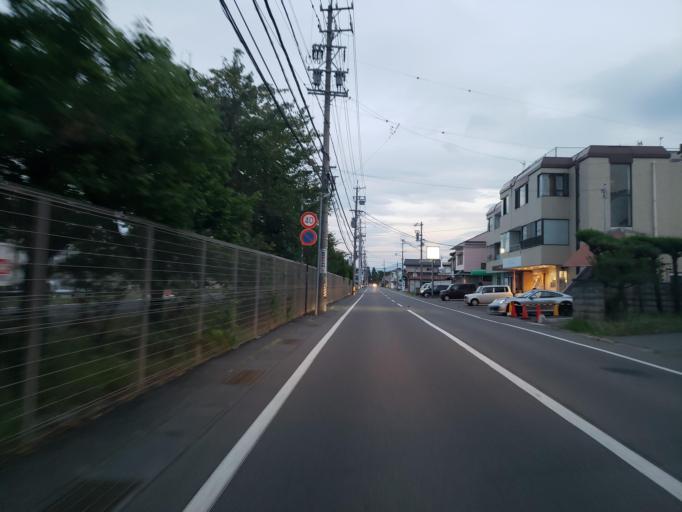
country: JP
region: Nagano
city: Nagano-shi
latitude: 36.6330
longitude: 138.1726
